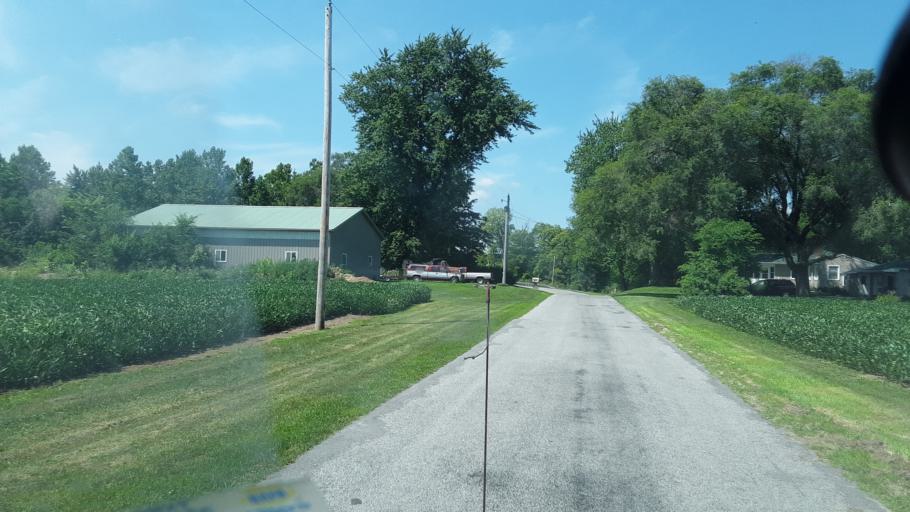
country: US
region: Ohio
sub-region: Hancock County
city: Findlay
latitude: 40.9766
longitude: -83.5370
